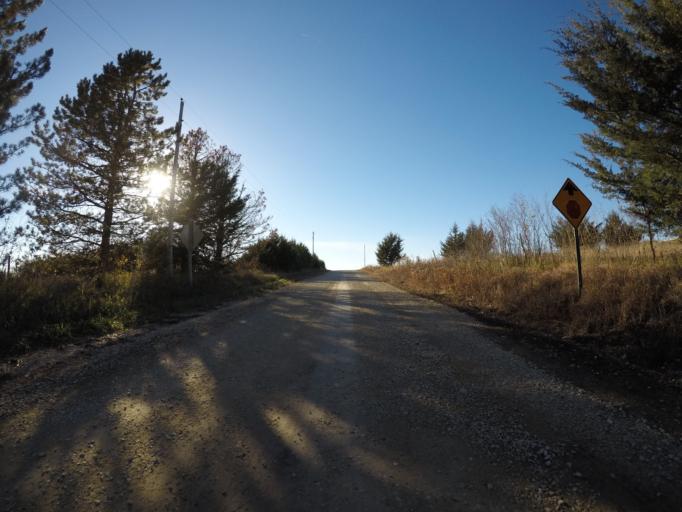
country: US
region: Kansas
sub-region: Riley County
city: Fort Riley North
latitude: 39.2620
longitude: -96.7731
